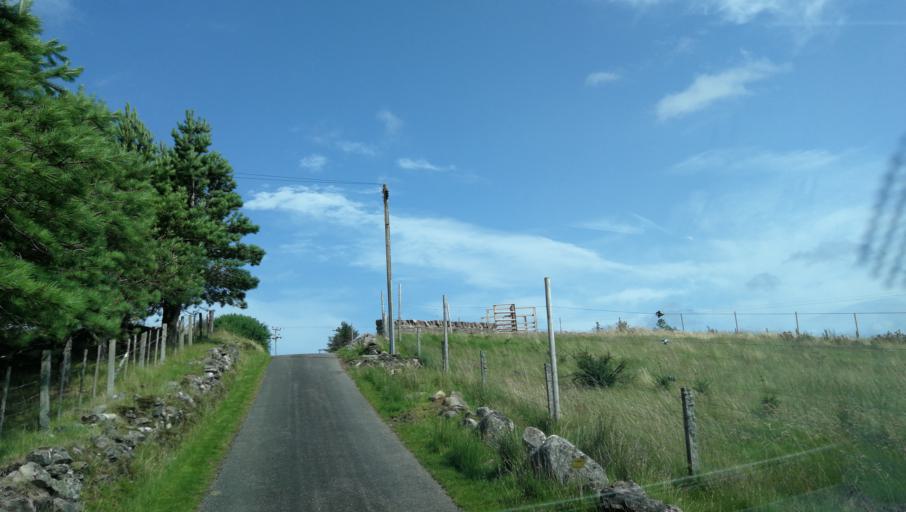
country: GB
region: Scotland
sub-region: Highland
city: Portree
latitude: 57.7445
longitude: -5.7756
